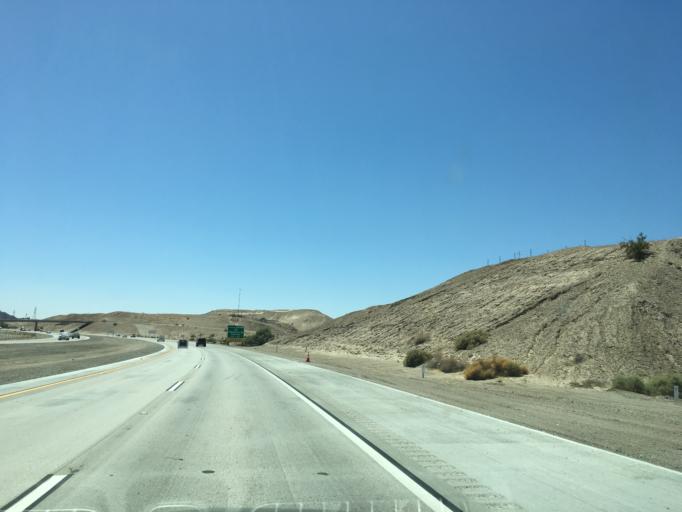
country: MX
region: Baja California
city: Los Algodones
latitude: 32.7474
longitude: -114.6983
